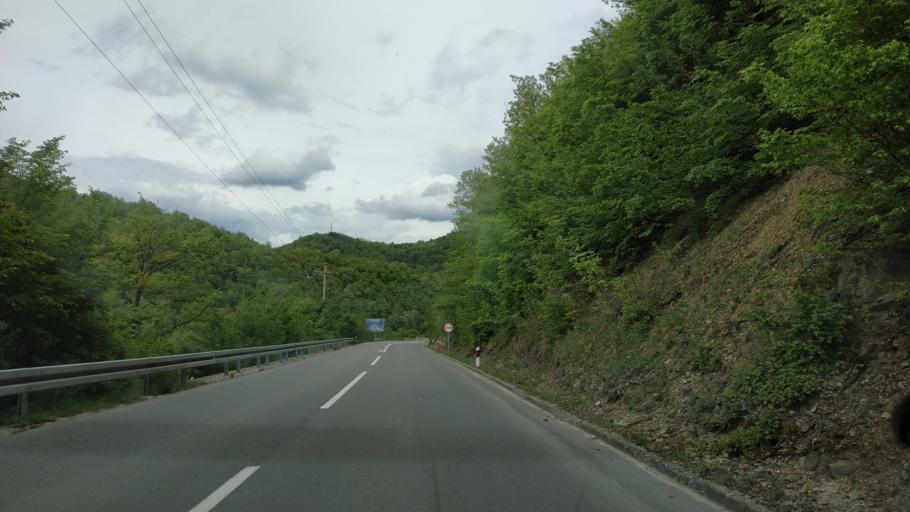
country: RS
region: Central Serbia
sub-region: Nisavski Okrug
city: Aleksinac
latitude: 43.6540
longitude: 21.7195
